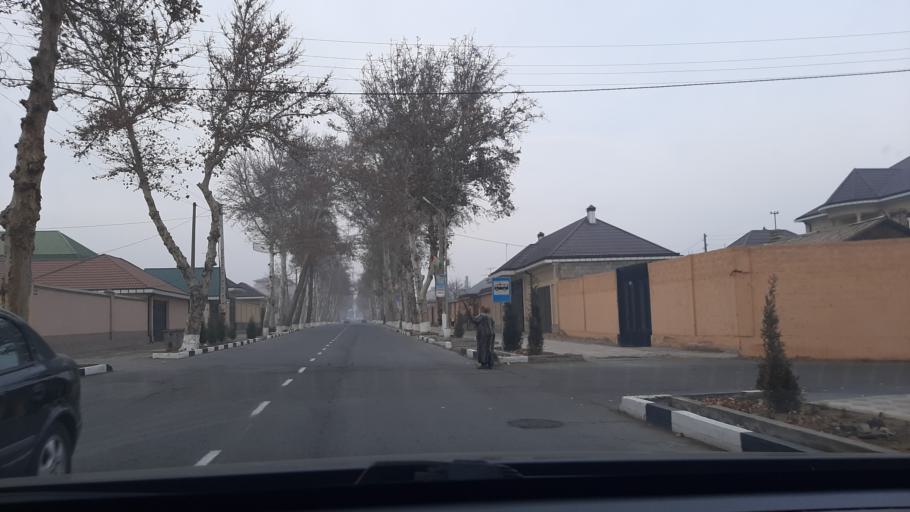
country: TJ
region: Viloyati Sughd
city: Chkalov
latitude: 40.2391
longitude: 69.6966
